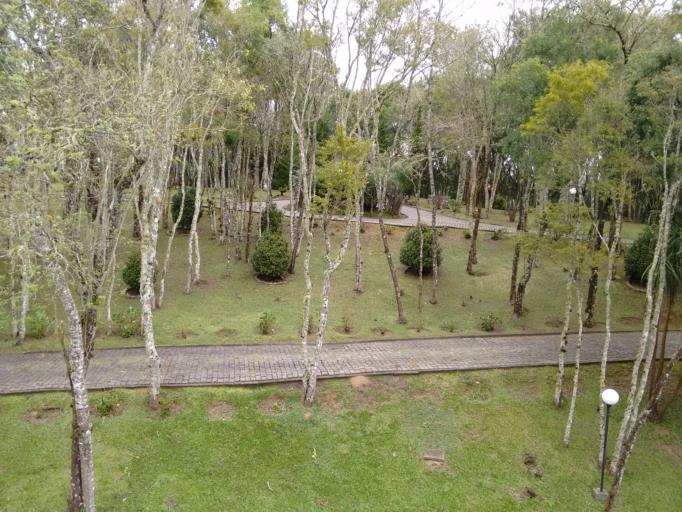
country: BR
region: Parana
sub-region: Campina Grande Do Sul
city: Campina Grande do Sul
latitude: -25.1881
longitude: -48.8727
